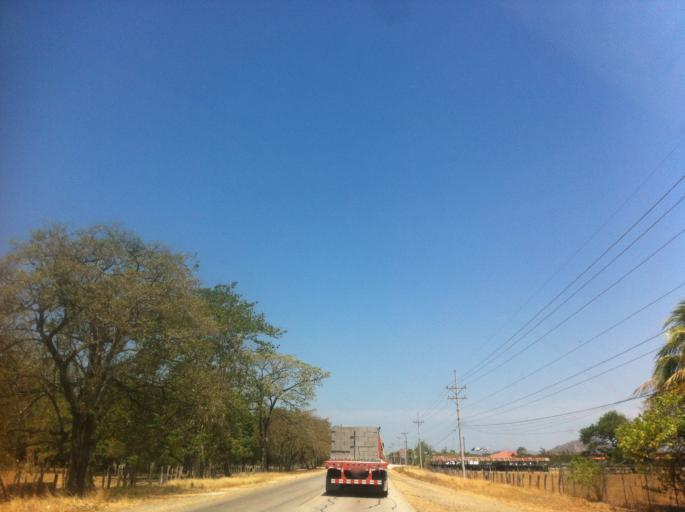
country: CR
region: Guanacaste
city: Santa Cruz
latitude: 10.2446
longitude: -85.5560
